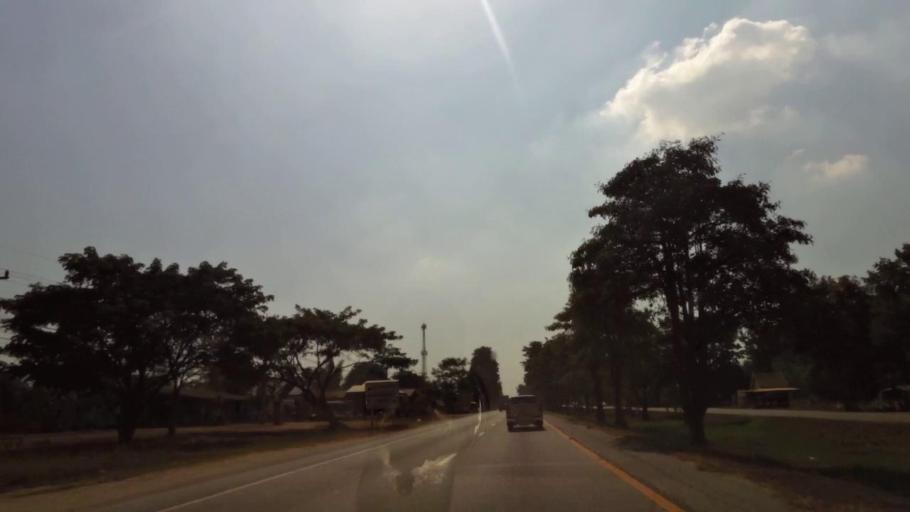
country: TH
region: Phichit
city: Wachira Barami
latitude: 16.5341
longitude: 100.1439
